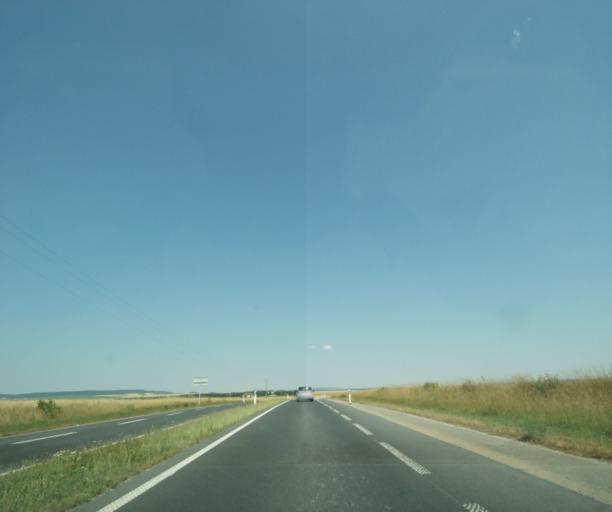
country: FR
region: Champagne-Ardenne
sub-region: Departement de la Marne
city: Mourmelon-le-Grand
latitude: 49.0763
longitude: 4.2863
